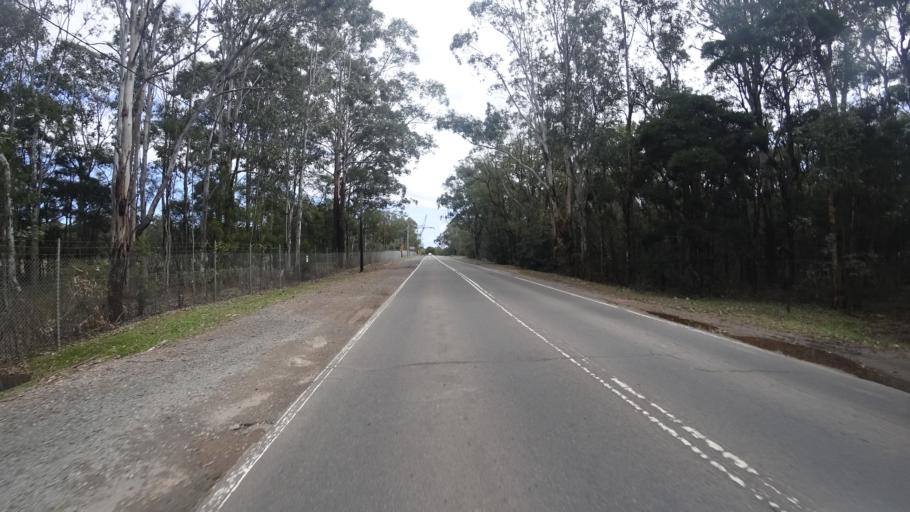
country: AU
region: New South Wales
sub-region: Campbelltown Municipality
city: Glenfield
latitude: -33.9712
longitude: 150.9166
